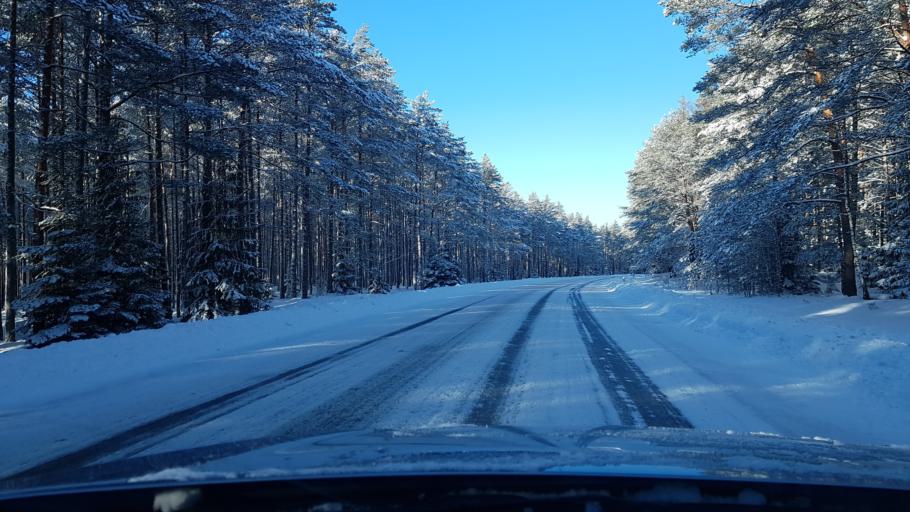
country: EE
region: Hiiumaa
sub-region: Kaerdla linn
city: Kardla
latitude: 58.9266
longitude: 22.7871
